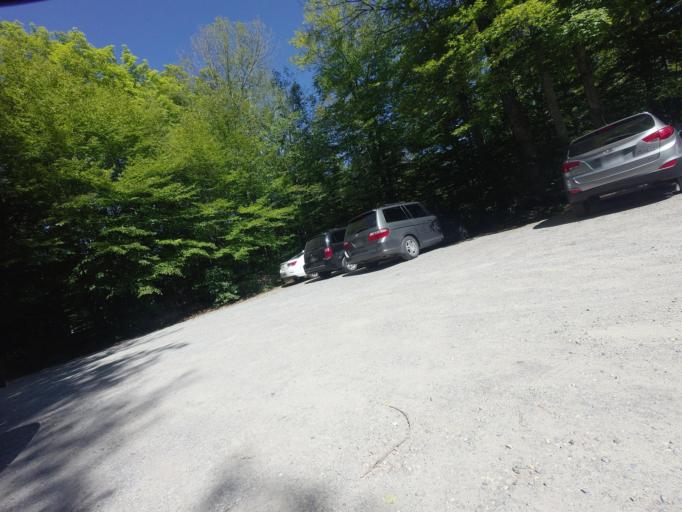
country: CA
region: Ontario
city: Renfrew
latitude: 45.3918
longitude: -76.5693
